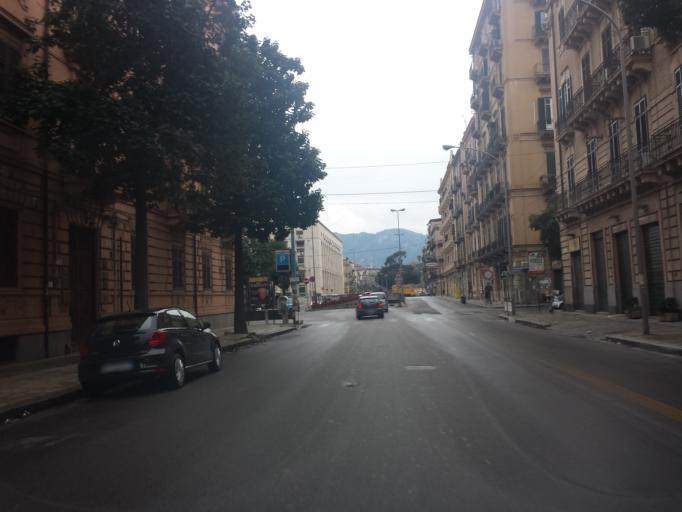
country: IT
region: Sicily
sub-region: Palermo
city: Palermo
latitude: 38.1202
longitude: 13.3507
